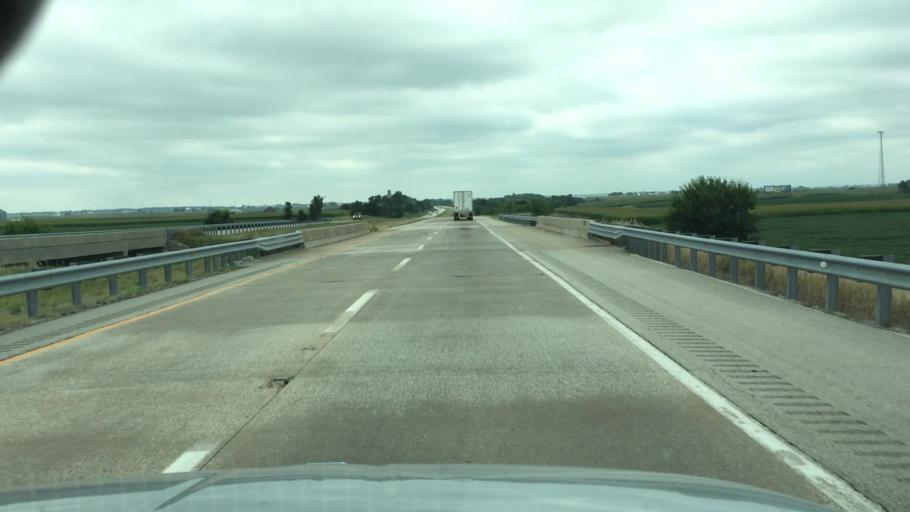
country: US
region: Illinois
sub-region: Henry County
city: Orion
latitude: 41.3469
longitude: -90.3327
